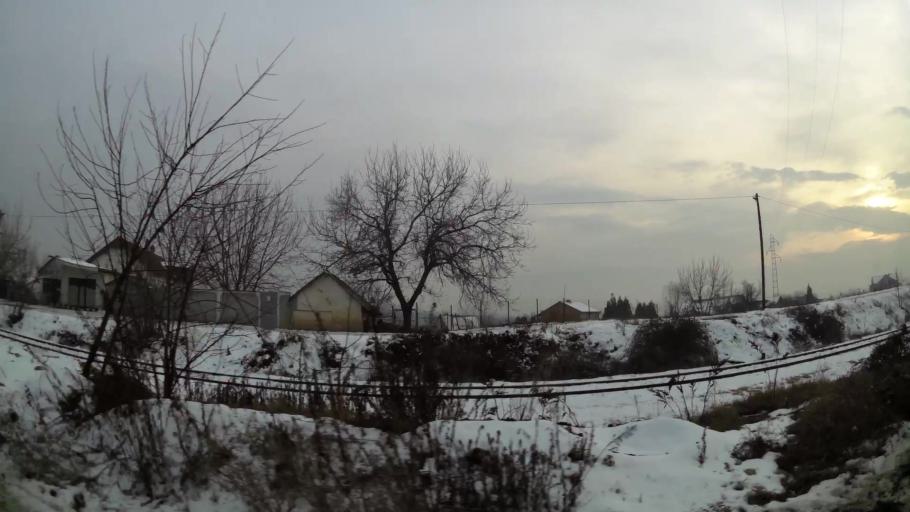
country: MK
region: Suto Orizari
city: Suto Orizare
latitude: 42.0276
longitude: 21.4137
